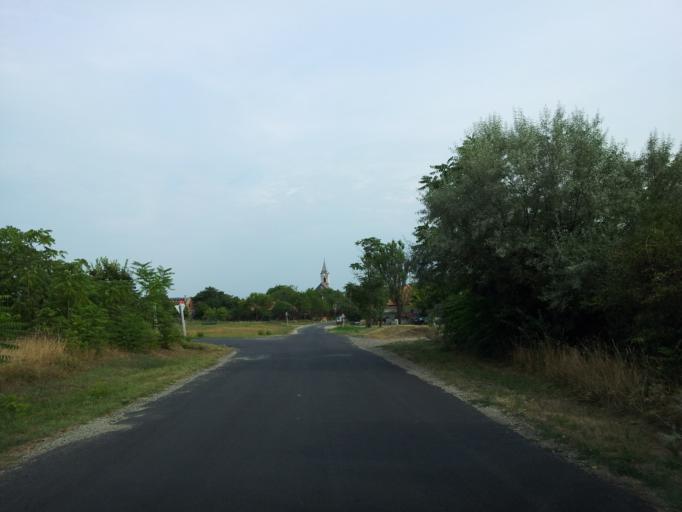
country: HU
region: Veszprem
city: Balatonfured
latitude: 46.9323
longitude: 17.8286
